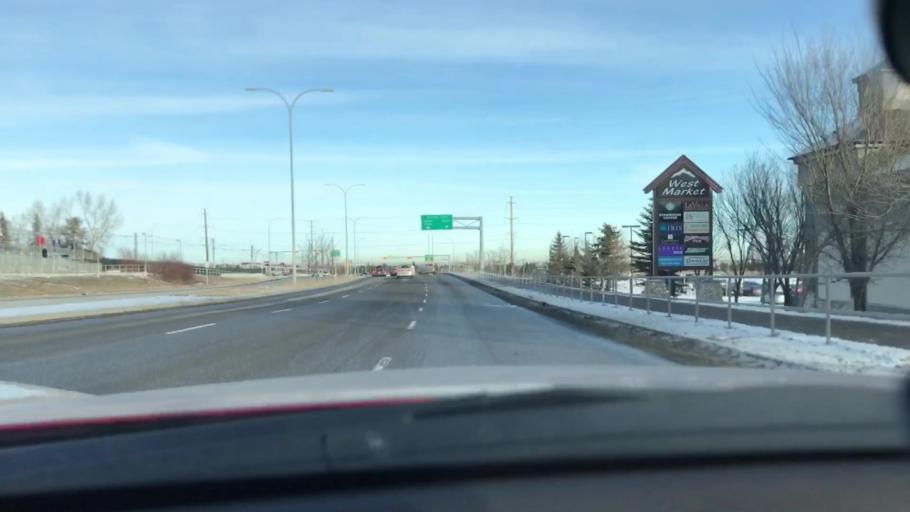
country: CA
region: Alberta
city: Calgary
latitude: 51.0379
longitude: -114.1689
